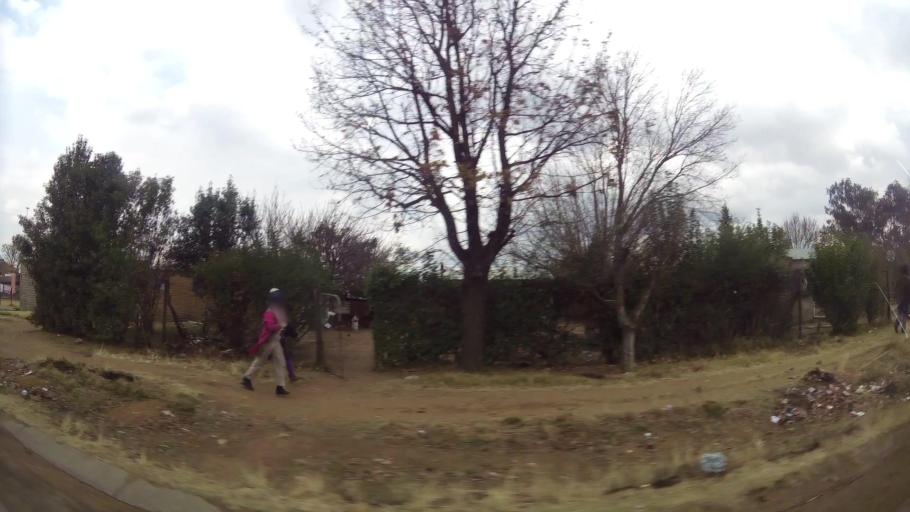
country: ZA
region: Orange Free State
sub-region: Fezile Dabi District Municipality
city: Sasolburg
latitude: -26.8478
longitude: 27.8766
